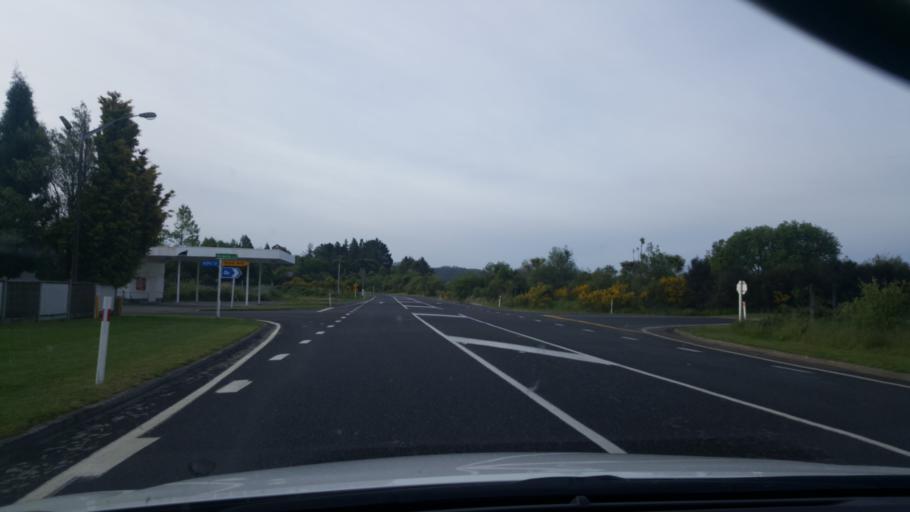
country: NZ
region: Waikato
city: Turangi
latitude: -38.9632
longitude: 175.7656
